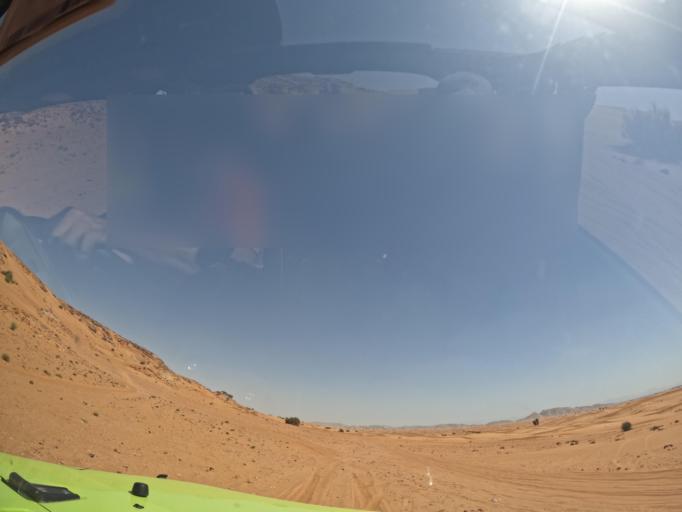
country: AE
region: Ash Shariqah
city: Adh Dhayd
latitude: 25.0180
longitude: 55.7280
